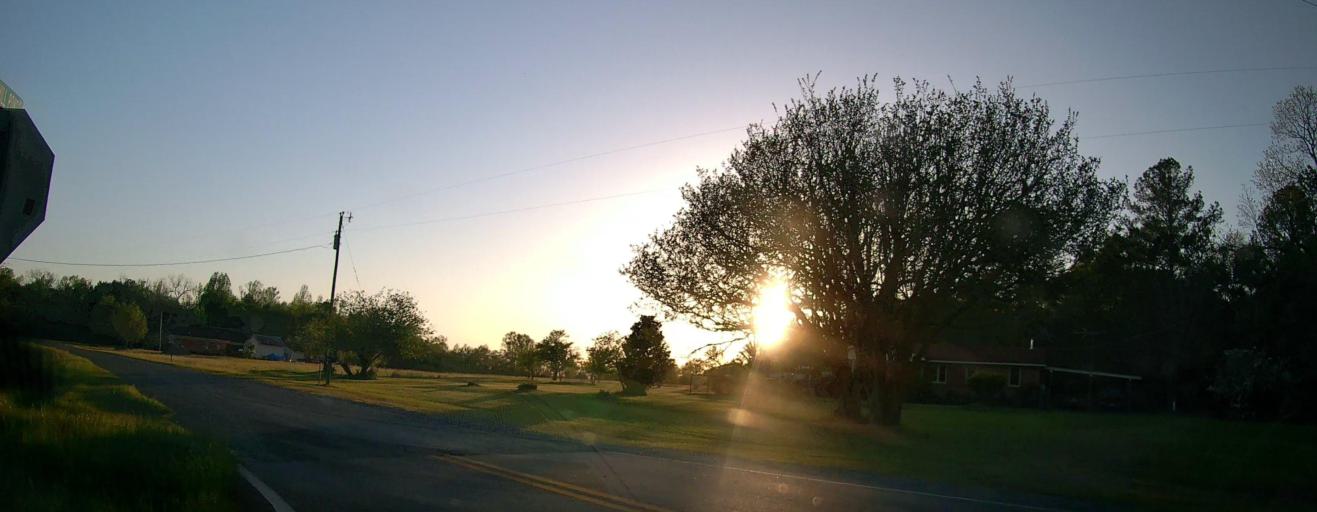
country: US
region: Georgia
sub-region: Talbot County
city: Talbotton
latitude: 32.5429
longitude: -84.5703
